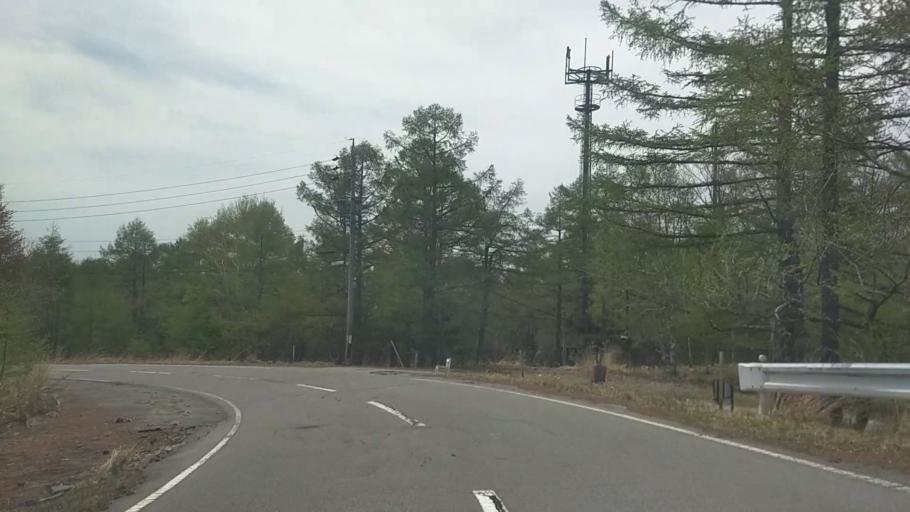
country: JP
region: Nagano
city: Chino
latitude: 36.0536
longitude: 138.3113
